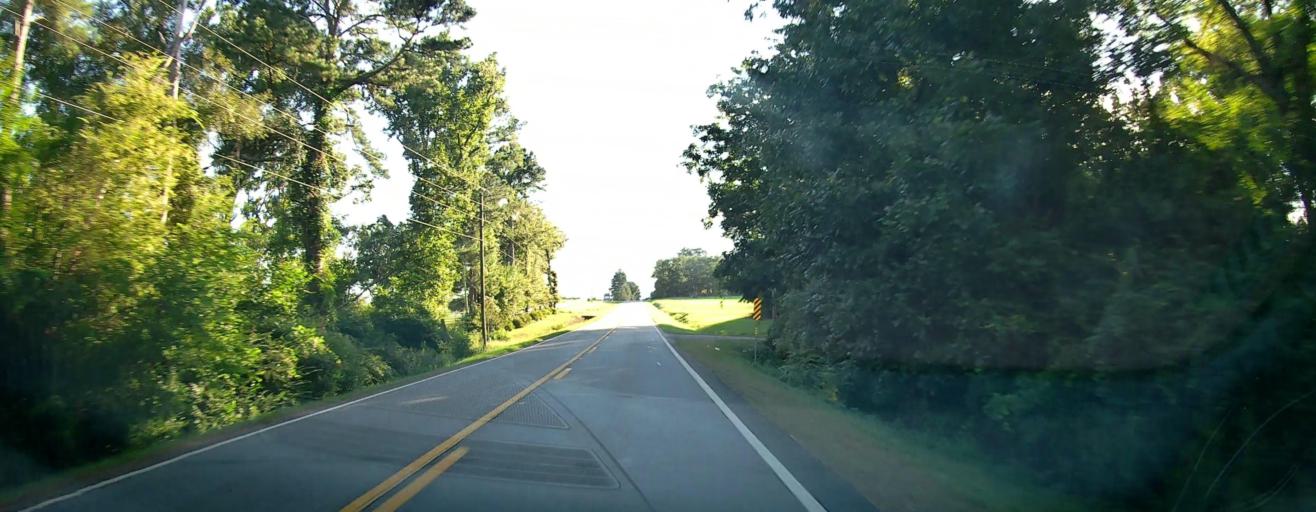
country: US
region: Georgia
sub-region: Pulaski County
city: Hawkinsville
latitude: 32.2688
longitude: -83.5099
